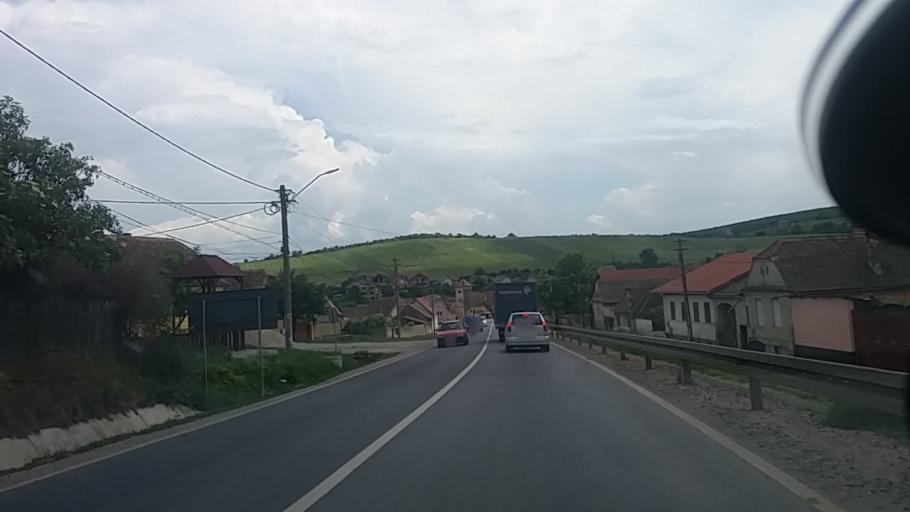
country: RO
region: Sibiu
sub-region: Comuna Sura Mare
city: Sura Mare
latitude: 45.8561
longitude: 24.1698
